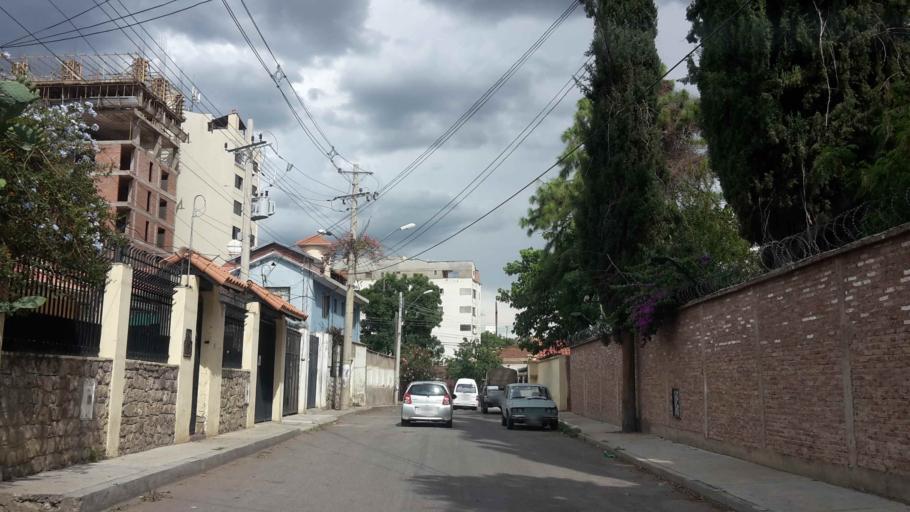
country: BO
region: Cochabamba
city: Cochabamba
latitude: -17.3675
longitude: -66.1667
